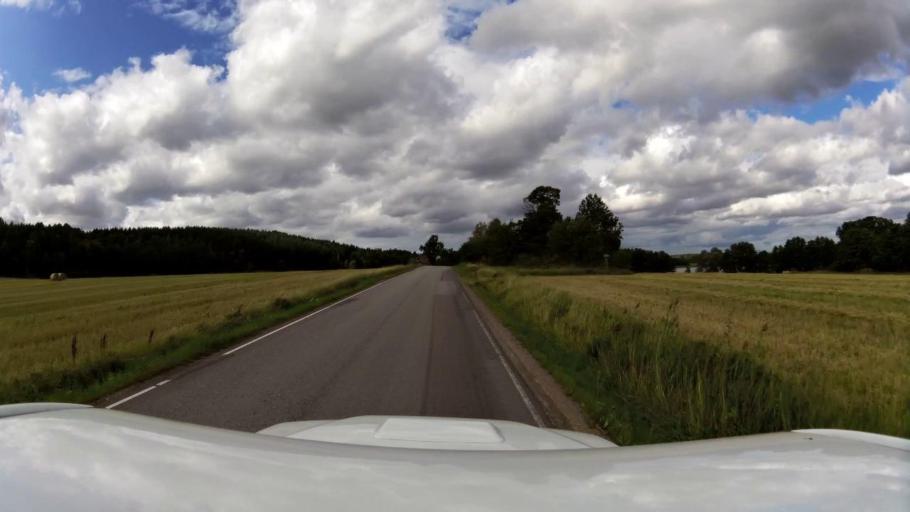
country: SE
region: OEstergoetland
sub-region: Linkopings Kommun
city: Sturefors
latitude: 58.3176
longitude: 15.7213
